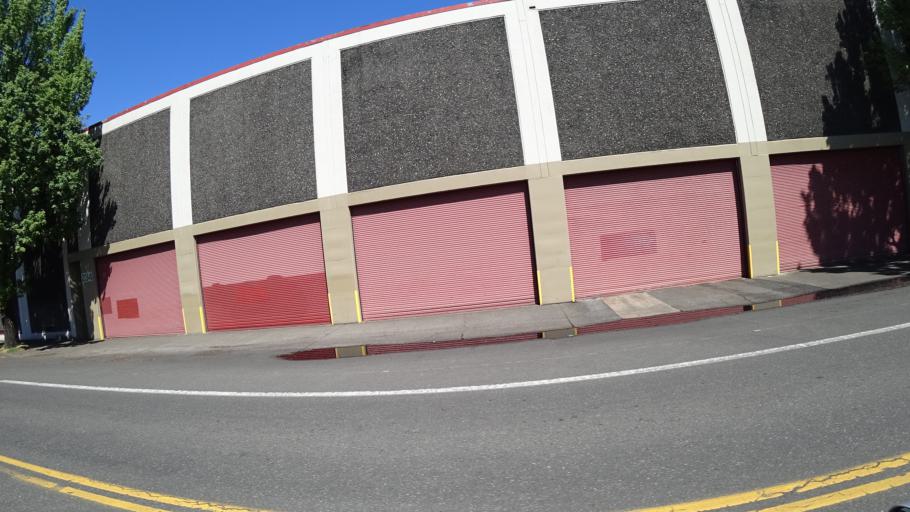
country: US
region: Oregon
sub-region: Multnomah County
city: Portland
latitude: 45.5248
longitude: -122.6536
